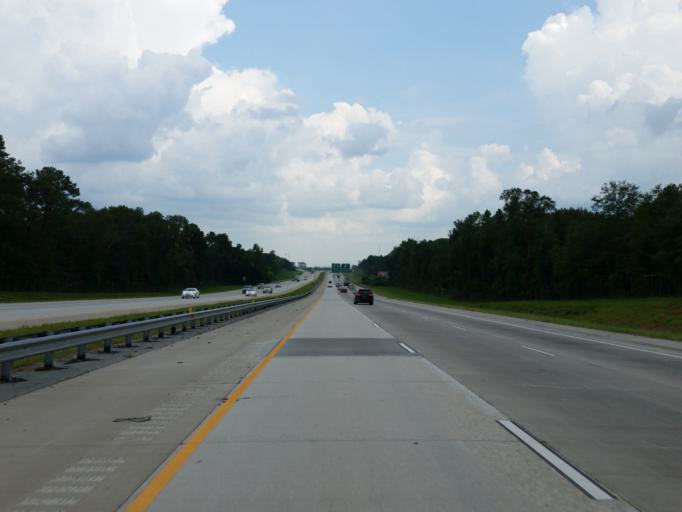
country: US
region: Georgia
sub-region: Dooly County
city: Unadilla
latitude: 32.2727
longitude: -83.7535
